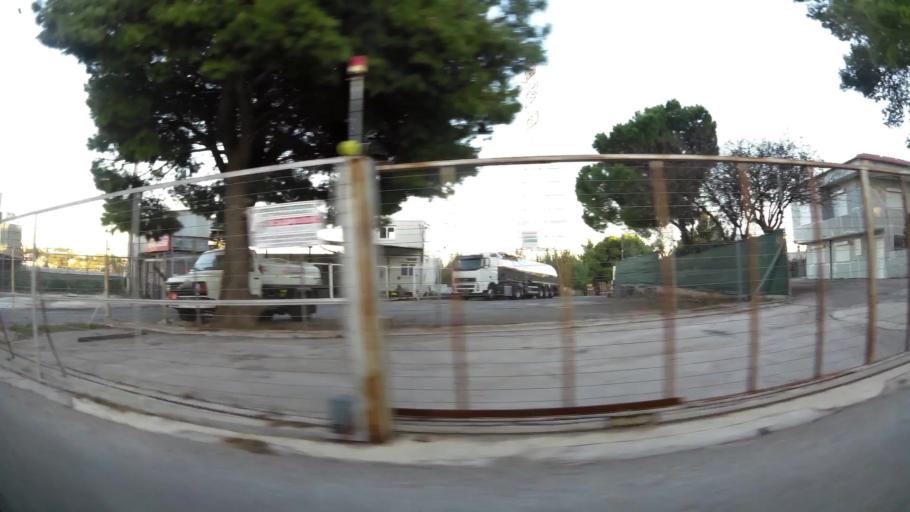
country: GR
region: Attica
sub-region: Nomarchia Anatolikis Attikis
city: Kryoneri
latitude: 38.1392
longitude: 23.8376
